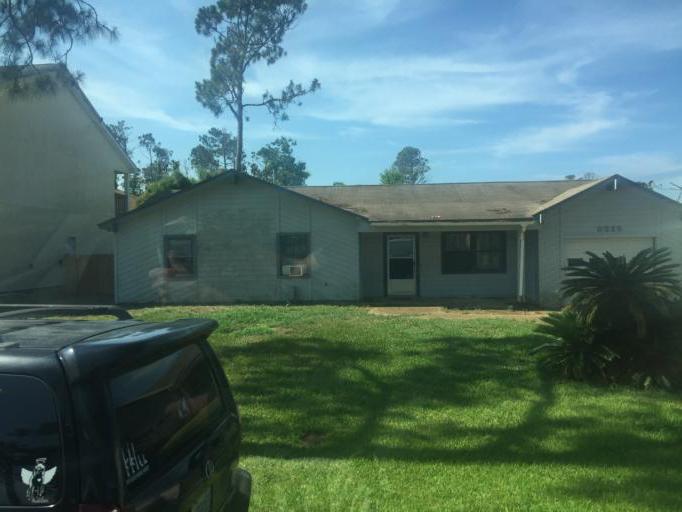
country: US
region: Florida
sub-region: Bay County
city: Lower Grand Lagoon
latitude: 30.1589
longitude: -85.7561
